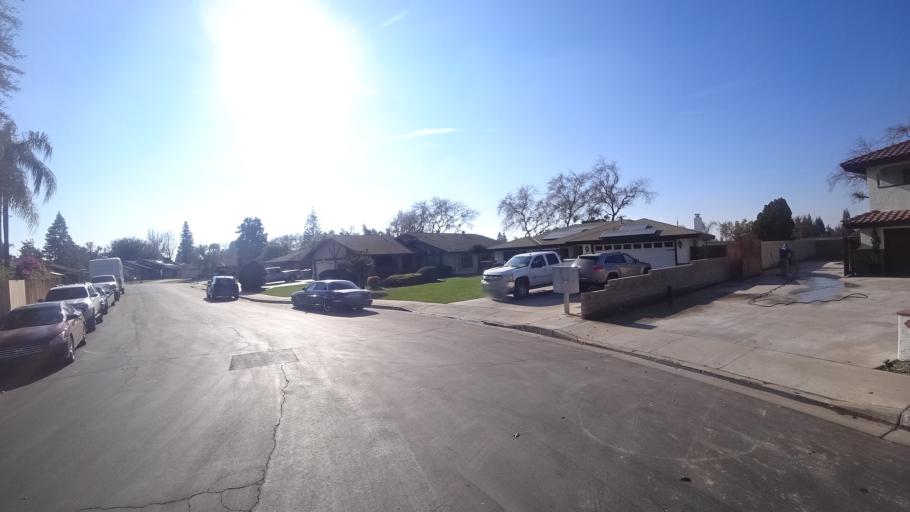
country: US
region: California
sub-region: Kern County
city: Greenacres
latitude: 35.3245
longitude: -119.1085
